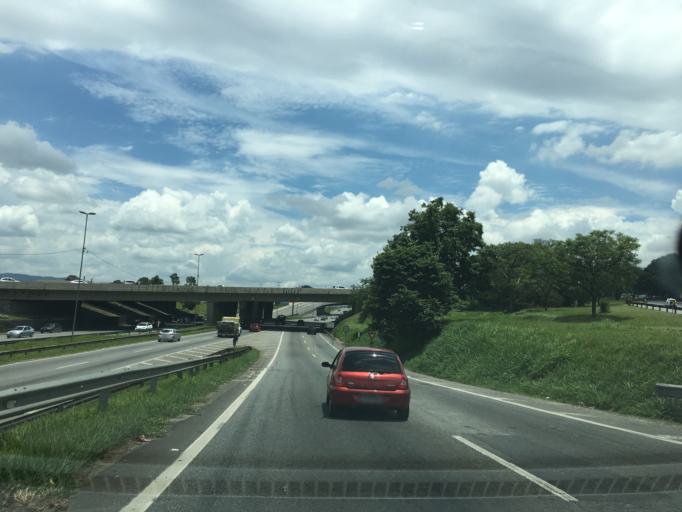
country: BR
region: Sao Paulo
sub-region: Guarulhos
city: Guarulhos
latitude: -23.4997
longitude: -46.5591
